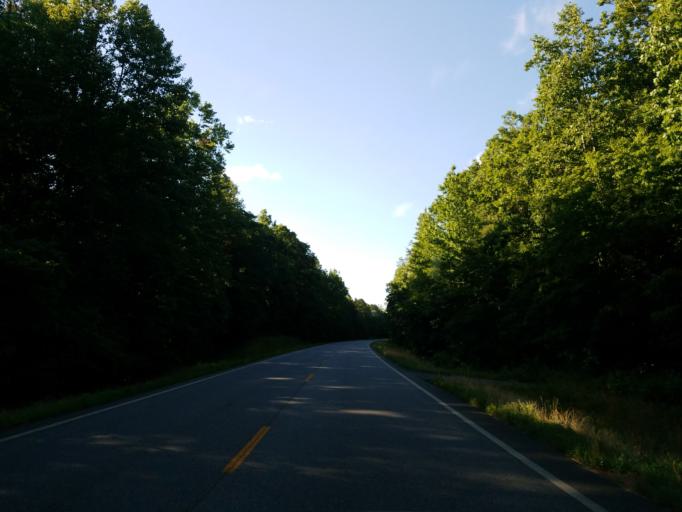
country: US
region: Georgia
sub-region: Whitfield County
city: Dalton
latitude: 34.6428
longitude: -85.0610
